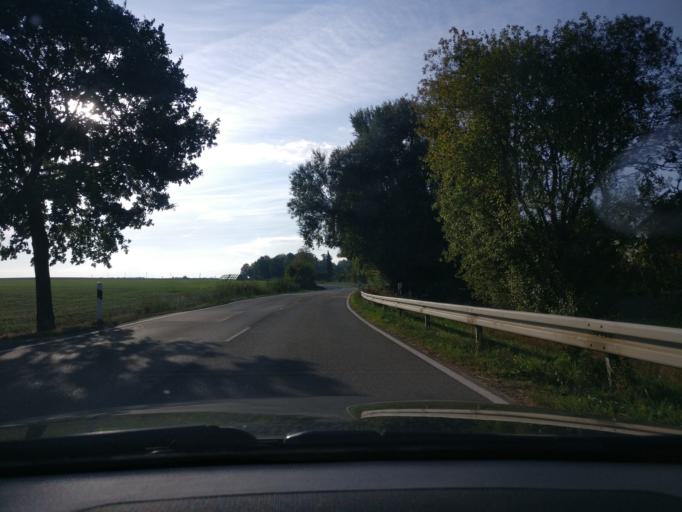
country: DE
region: Lower Saxony
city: Melle
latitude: 52.1977
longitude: 8.2598
